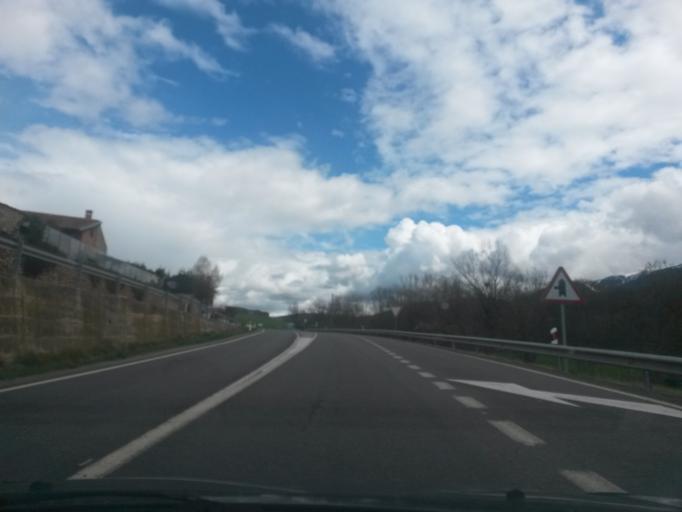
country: ES
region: Catalonia
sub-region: Provincia de Girona
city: Isovol
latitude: 42.3628
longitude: 1.8065
